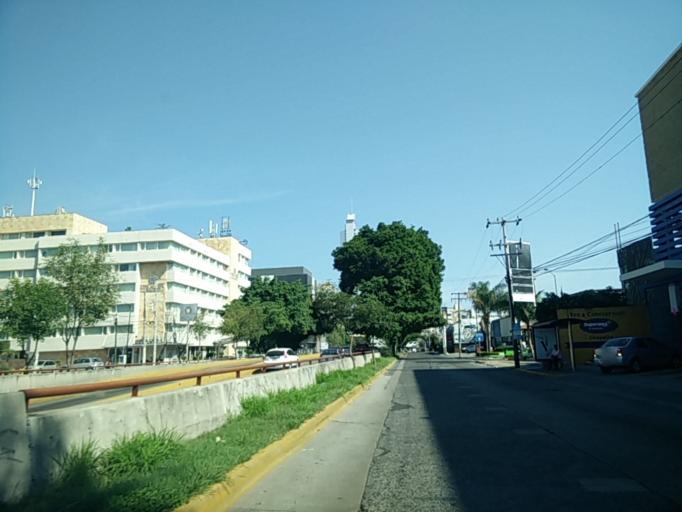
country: MX
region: Jalisco
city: Guadalajara
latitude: 20.6602
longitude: -103.3966
